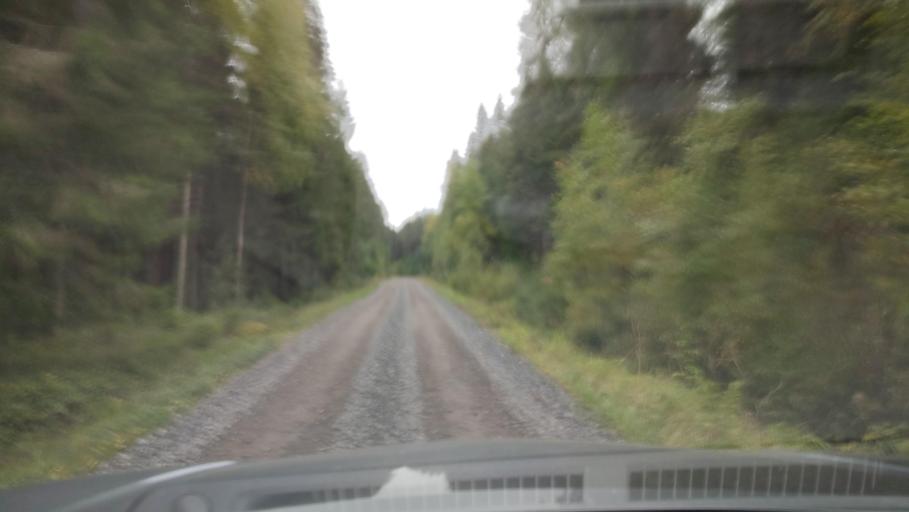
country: FI
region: Southern Ostrobothnia
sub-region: Suupohja
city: Karijoki
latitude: 62.2117
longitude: 21.5725
